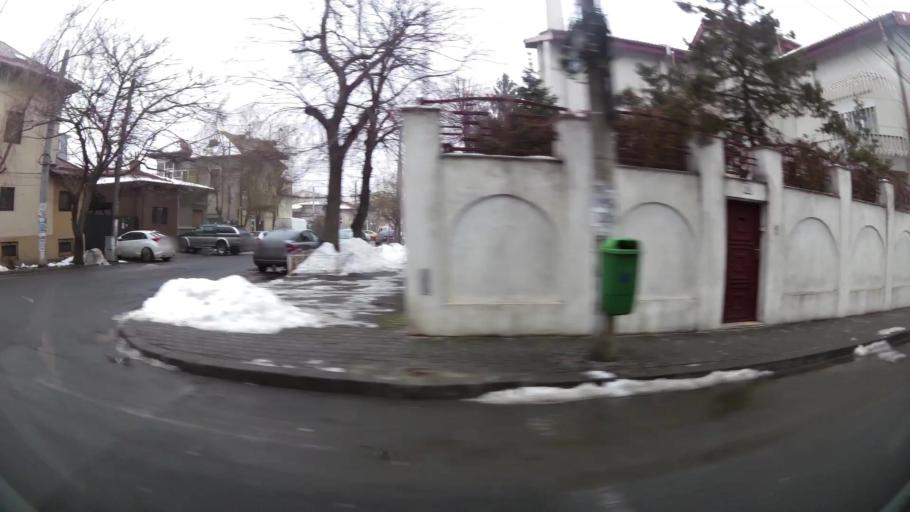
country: RO
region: Ilfov
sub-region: Comuna Chiajna
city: Rosu
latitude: 44.4497
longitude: 26.0553
